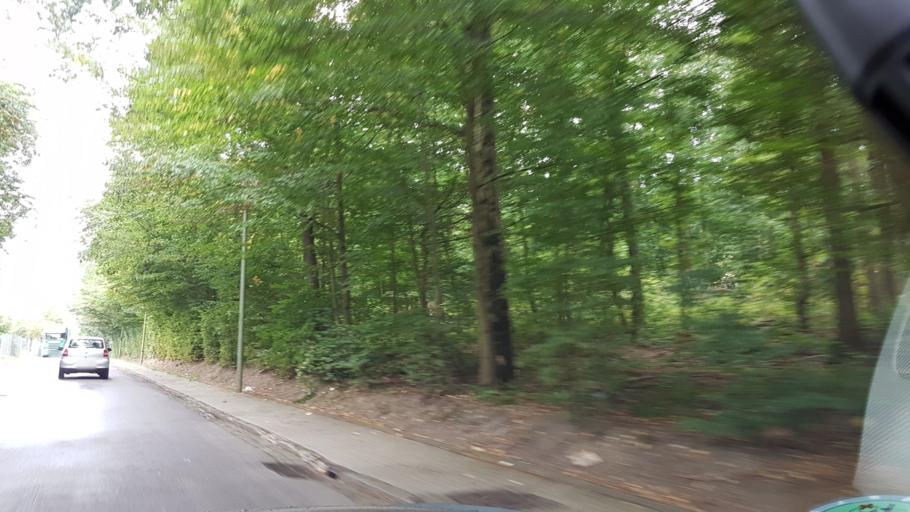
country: DE
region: Saarland
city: Sulzbach
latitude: 49.2894
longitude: 7.0643
